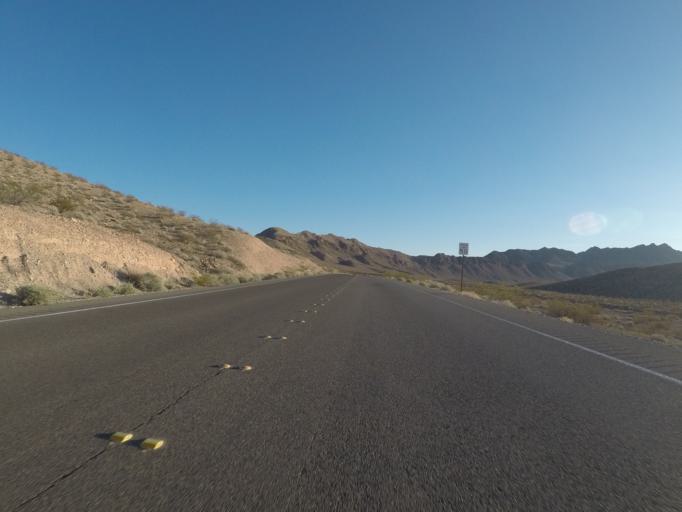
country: US
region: Nevada
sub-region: Clark County
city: Moapa Valley
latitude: 36.2665
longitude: -114.4828
